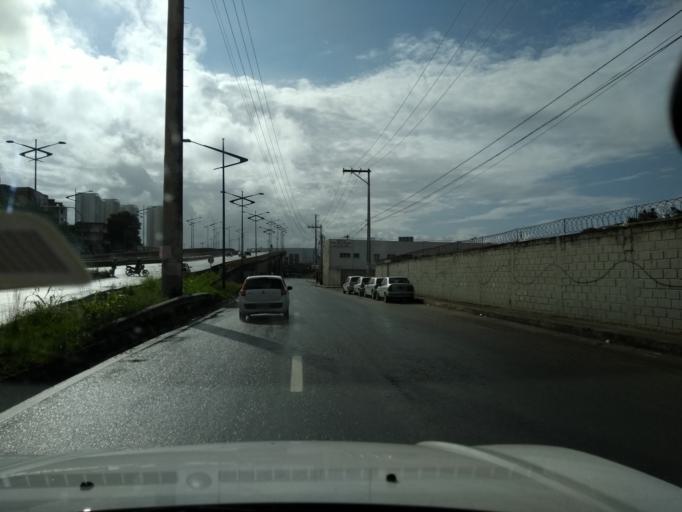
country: BR
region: Bahia
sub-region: Salvador
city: Salvador
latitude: -12.9690
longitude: -38.4831
